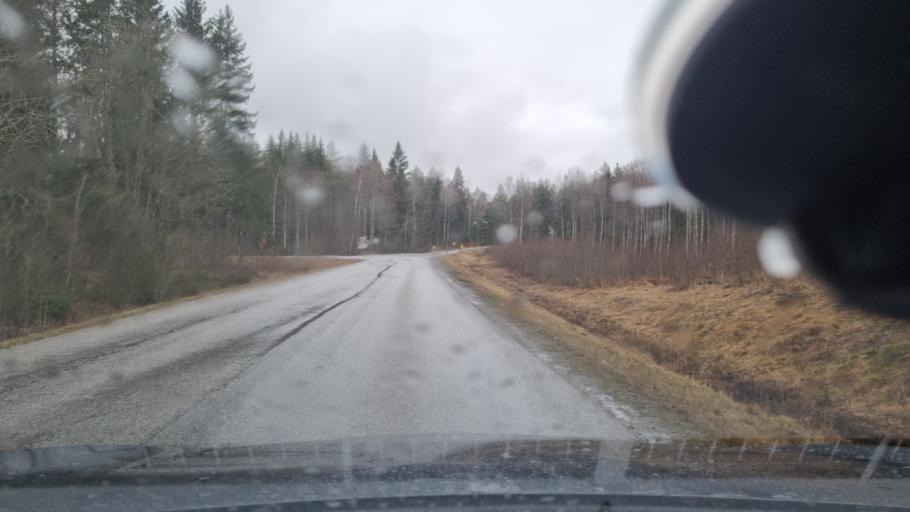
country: SE
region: Stockholm
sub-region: Sigtuna Kommun
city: Sigtuna
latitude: 59.5623
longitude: 17.7110
